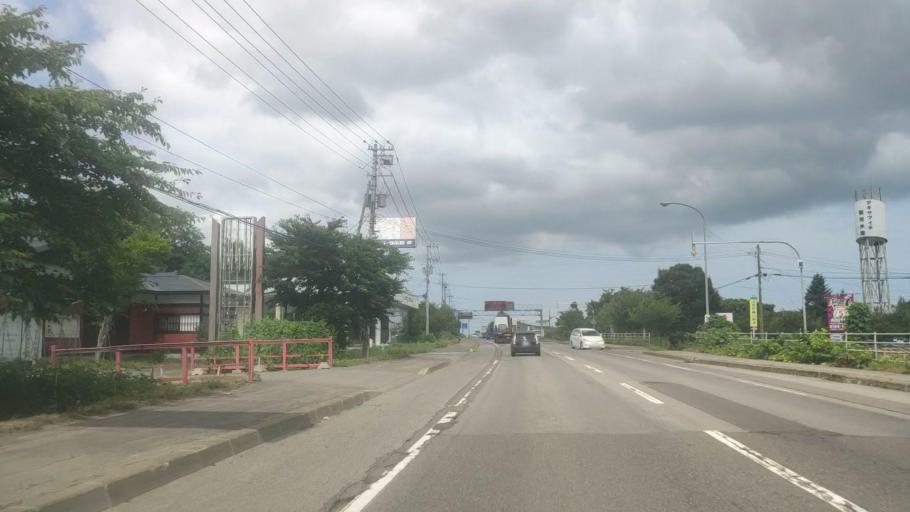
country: JP
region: Hokkaido
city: Nanae
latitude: 42.0901
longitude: 140.5806
